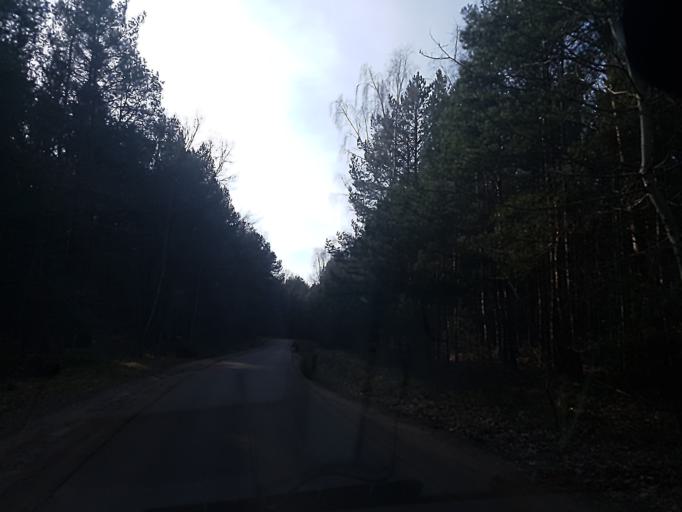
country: DE
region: Brandenburg
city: Wenzlow
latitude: 52.3477
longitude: 12.4613
